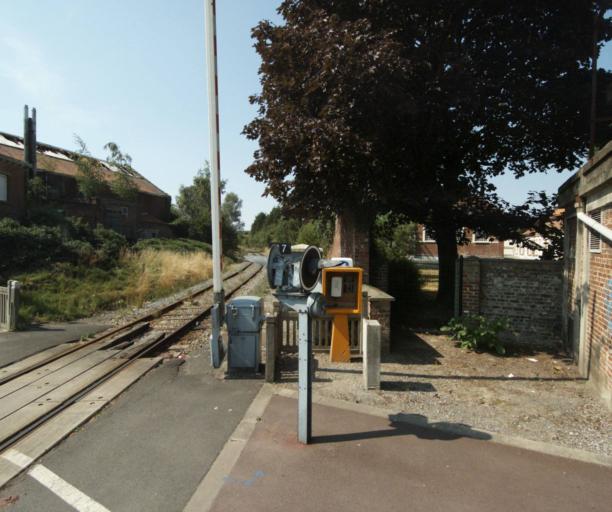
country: FR
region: Nord-Pas-de-Calais
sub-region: Departement du Nord
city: Comines
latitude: 50.7573
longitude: 3.0037
